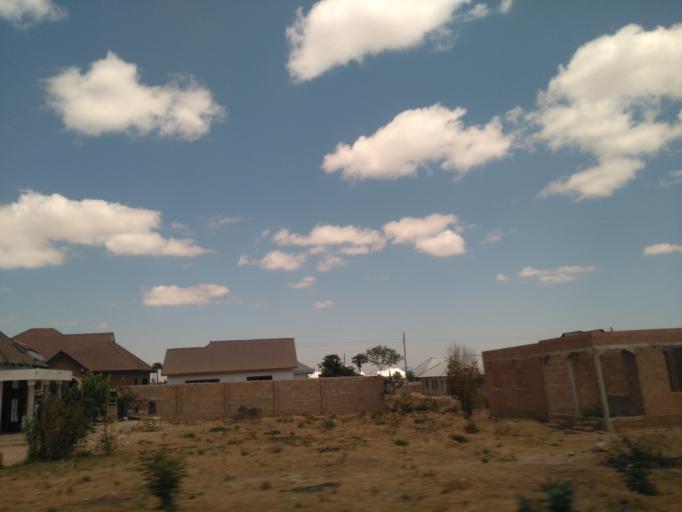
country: TZ
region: Dodoma
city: Kisasa
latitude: -6.1768
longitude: 35.7996
